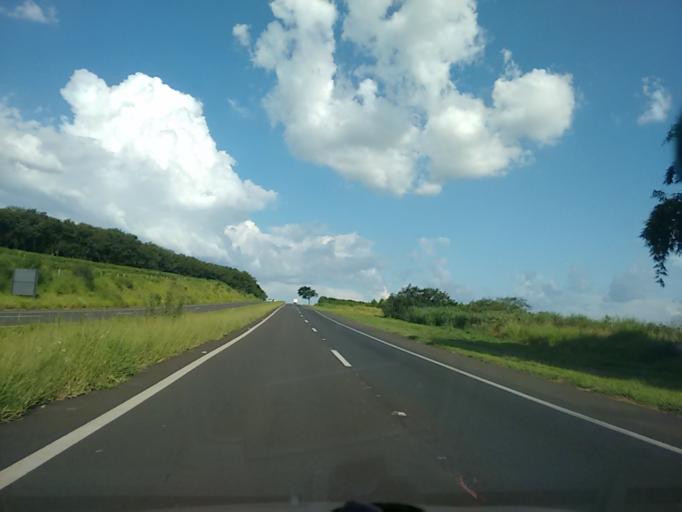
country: BR
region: Sao Paulo
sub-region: Duartina
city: Duartina
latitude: -22.3274
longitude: -49.4711
